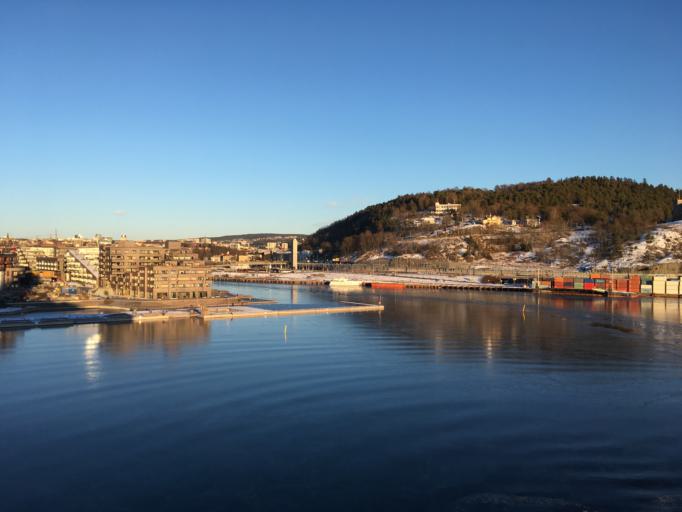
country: NO
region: Oslo
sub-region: Oslo
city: Oslo
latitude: 59.9001
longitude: 10.7473
